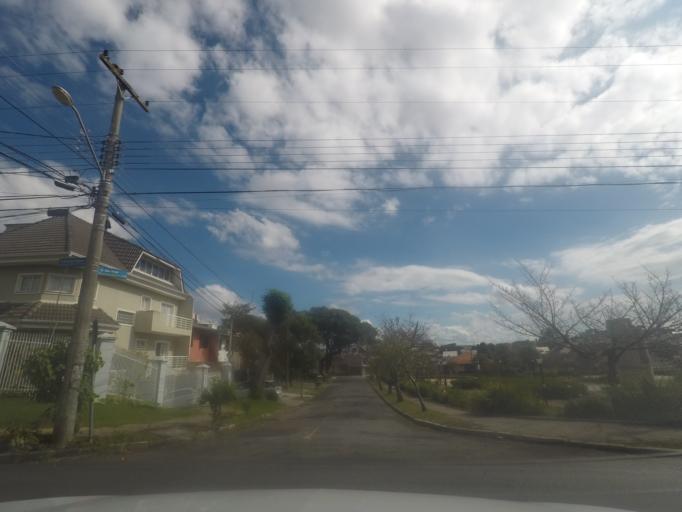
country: BR
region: Parana
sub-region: Pinhais
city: Pinhais
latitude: -25.4639
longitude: -49.2264
